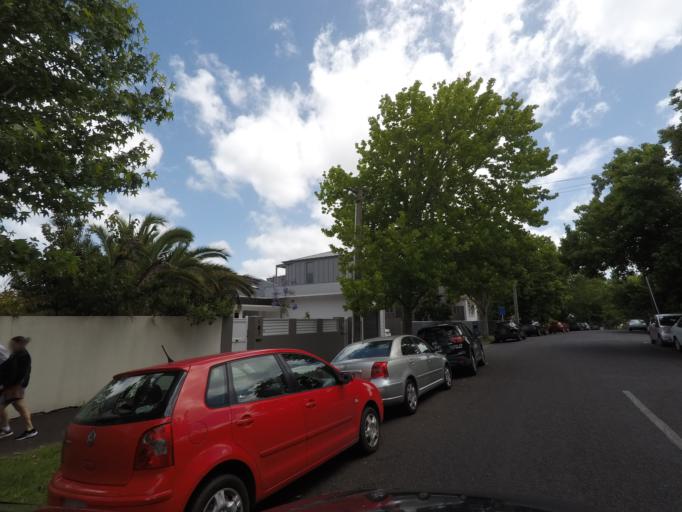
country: NZ
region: Auckland
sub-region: Auckland
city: Auckland
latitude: -36.8515
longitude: 174.7845
